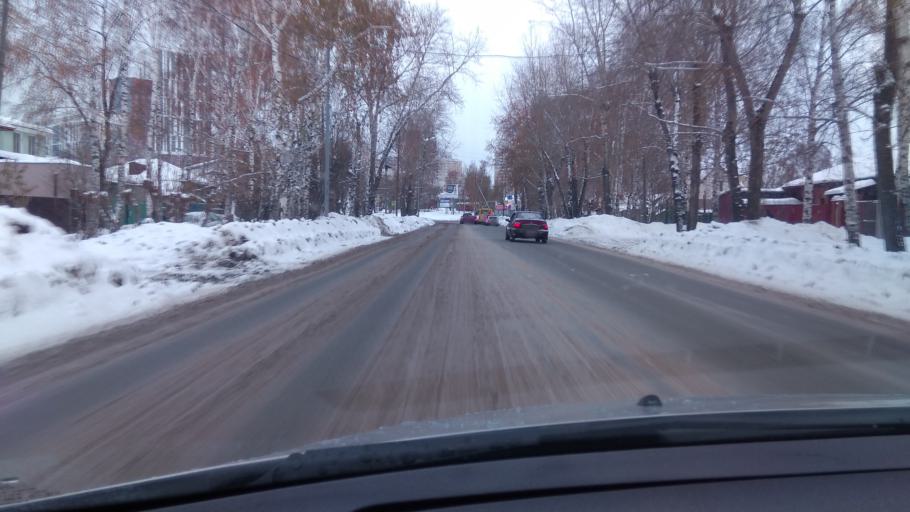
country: RU
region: Sverdlovsk
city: Yekaterinburg
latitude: 56.8075
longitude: 60.5892
